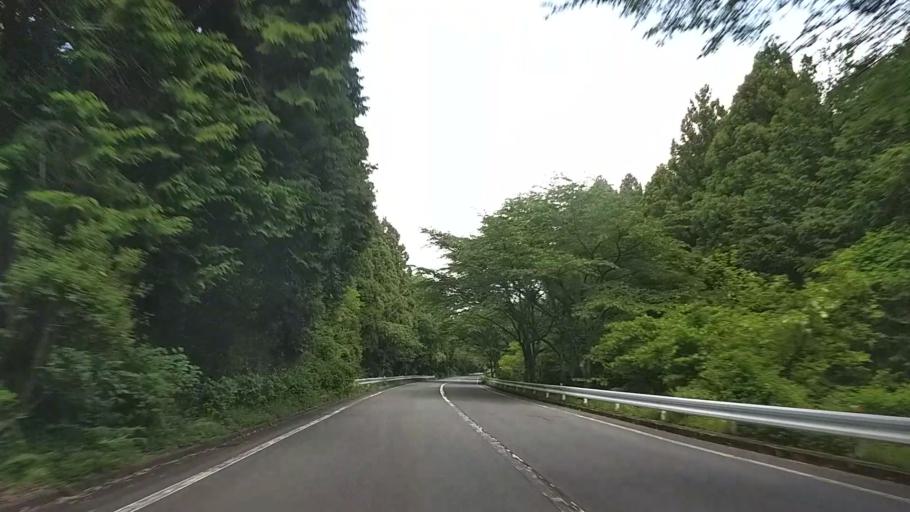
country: JP
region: Kanagawa
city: Odawara
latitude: 35.2261
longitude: 139.1177
